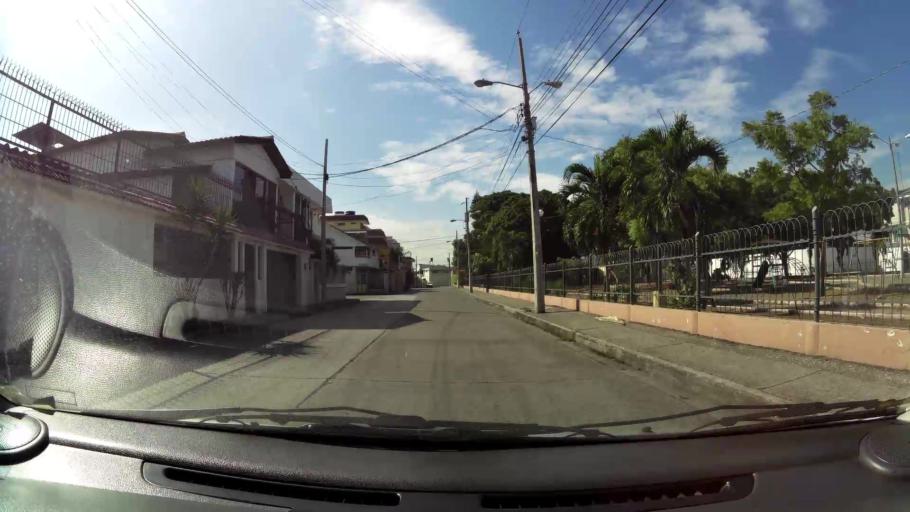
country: EC
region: Guayas
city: Guayaquil
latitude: -2.2299
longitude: -79.8943
